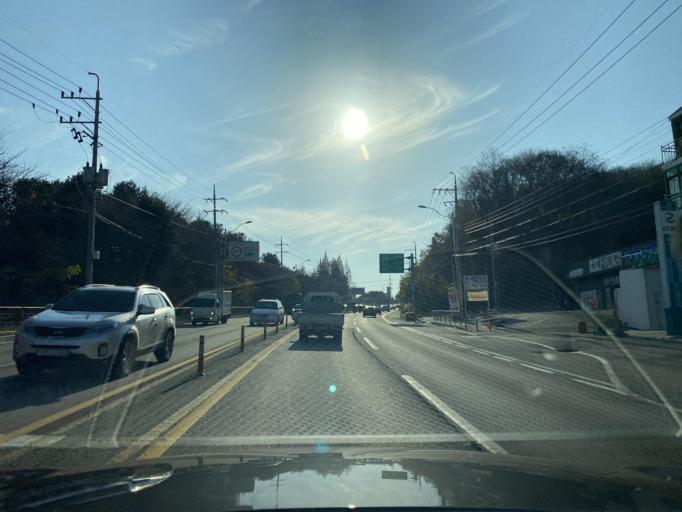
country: KR
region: Chungcheongnam-do
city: Asan
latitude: 36.7717
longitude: 126.9298
